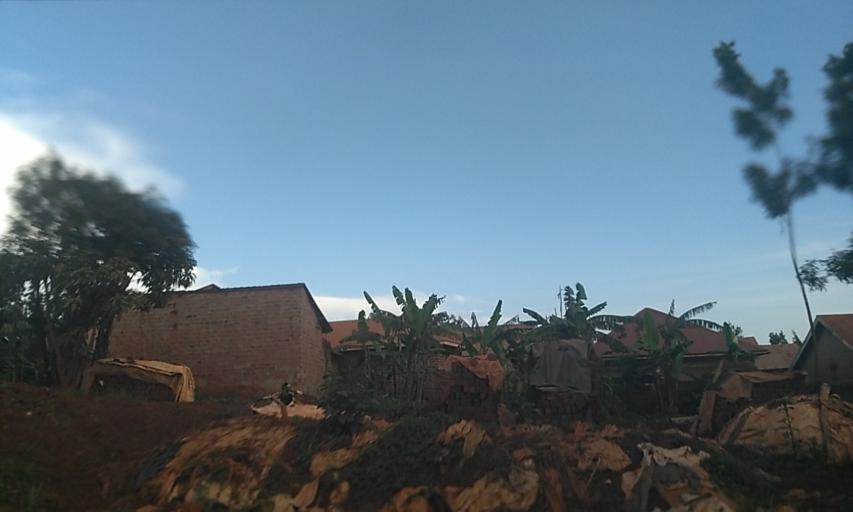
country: UG
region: Central Region
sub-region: Wakiso District
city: Kajansi
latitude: 0.2608
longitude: 32.5099
